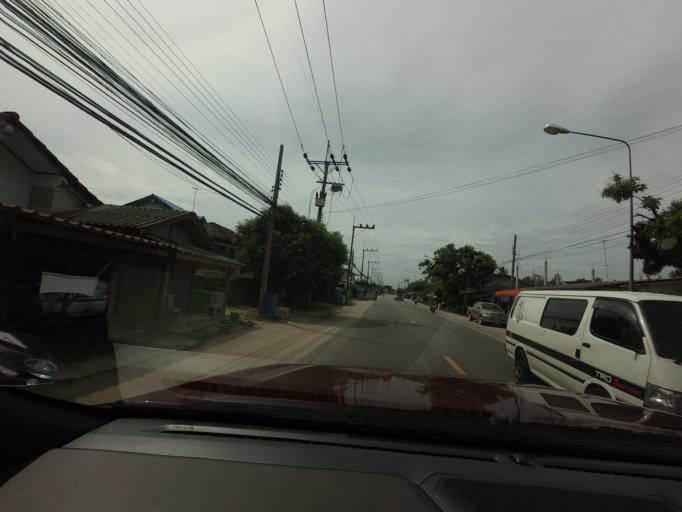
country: TH
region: Narathiwat
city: Tak Bai
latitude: 6.2535
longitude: 102.0624
